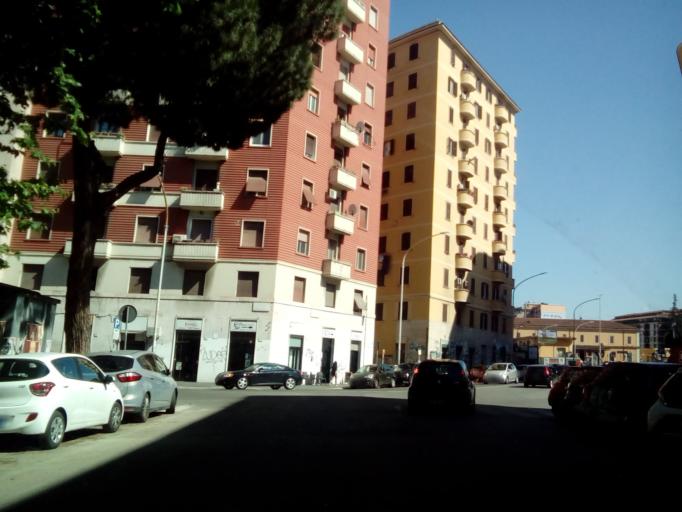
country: IT
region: Latium
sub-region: Citta metropolitana di Roma Capitale
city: Rome
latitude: 41.8811
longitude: 12.5223
